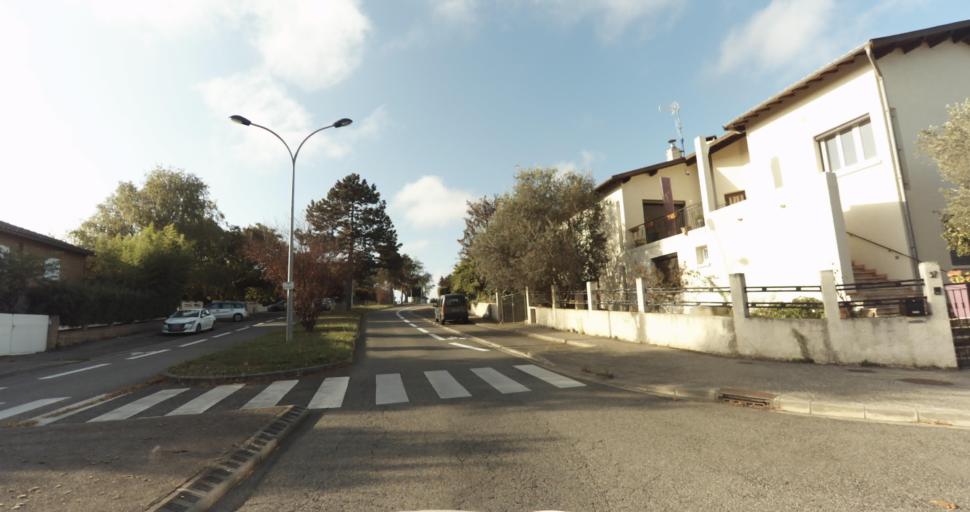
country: FR
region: Midi-Pyrenees
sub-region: Departement de la Haute-Garonne
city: Ramonville-Saint-Agne
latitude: 43.5460
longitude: 1.4647
